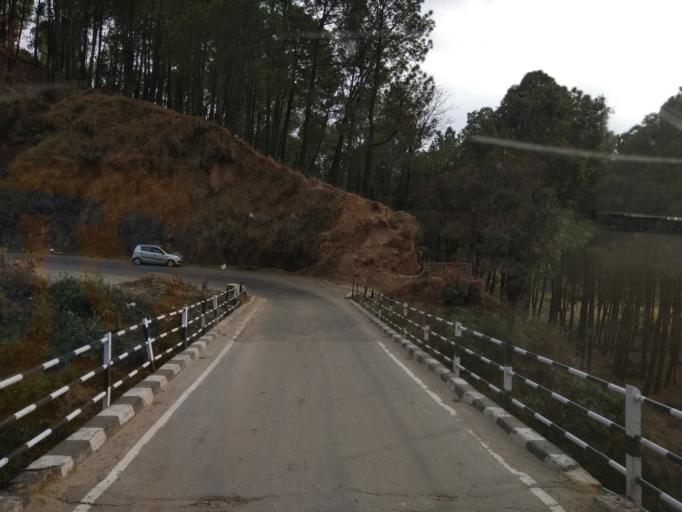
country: IN
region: Himachal Pradesh
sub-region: Kangra
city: Palampur
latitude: 32.1100
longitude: 76.4871
